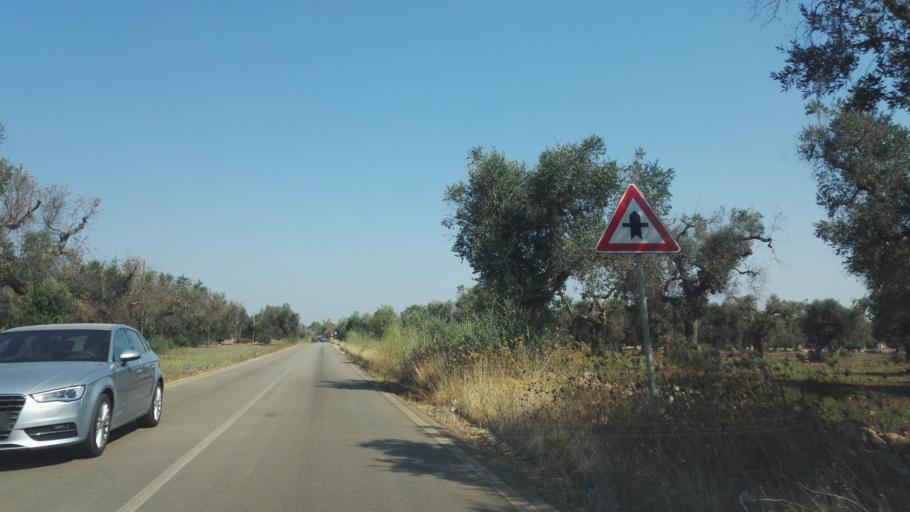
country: IT
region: Apulia
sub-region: Provincia di Lecce
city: Nardo
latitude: 40.1909
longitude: 17.9668
